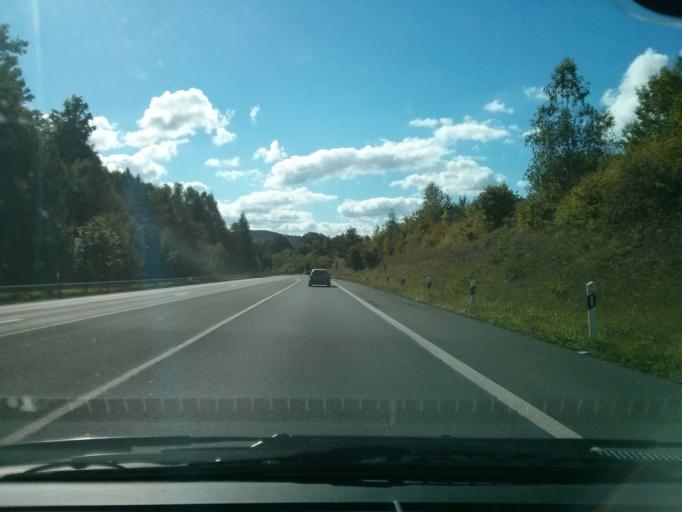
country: DE
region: North Rhine-Westphalia
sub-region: Regierungsbezirk Arnsberg
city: Arnsberg
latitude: 51.4218
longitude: 8.0576
